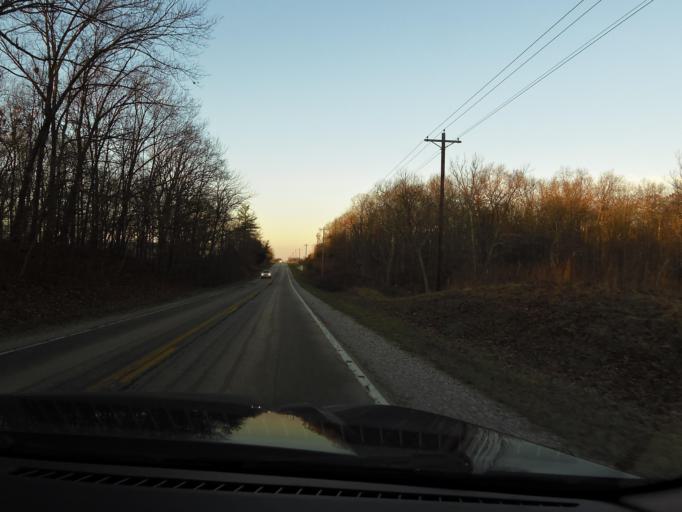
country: US
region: Illinois
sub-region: Marion County
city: Salem
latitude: 38.7654
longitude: -88.9618
